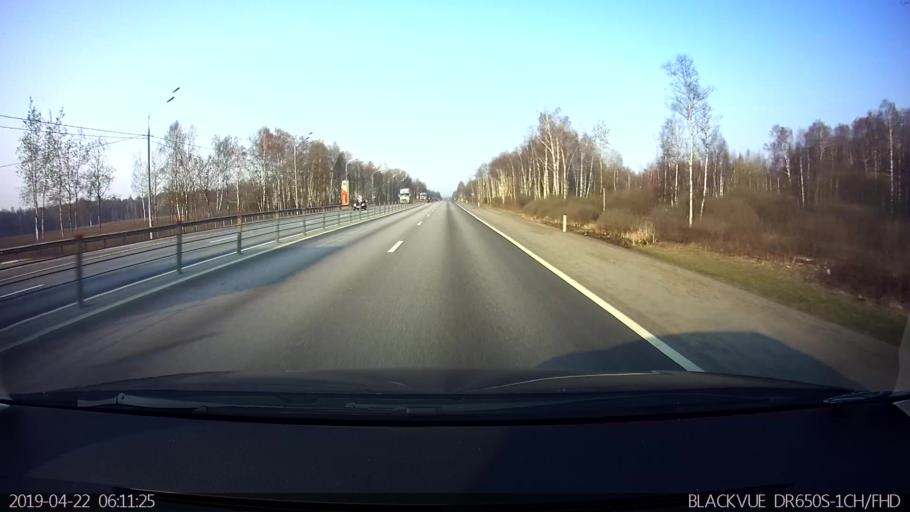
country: RU
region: Moskovskaya
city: Mozhaysk
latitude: 55.4866
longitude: 36.1497
